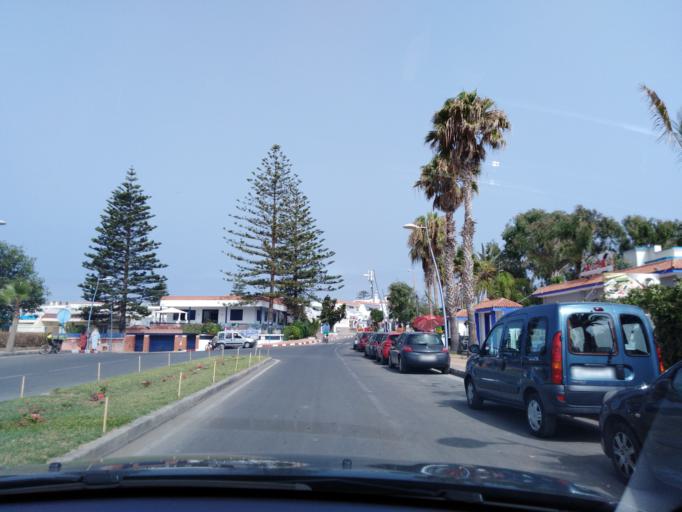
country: MA
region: Doukkala-Abda
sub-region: Safi
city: Safi
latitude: 32.7330
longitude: -9.0429
